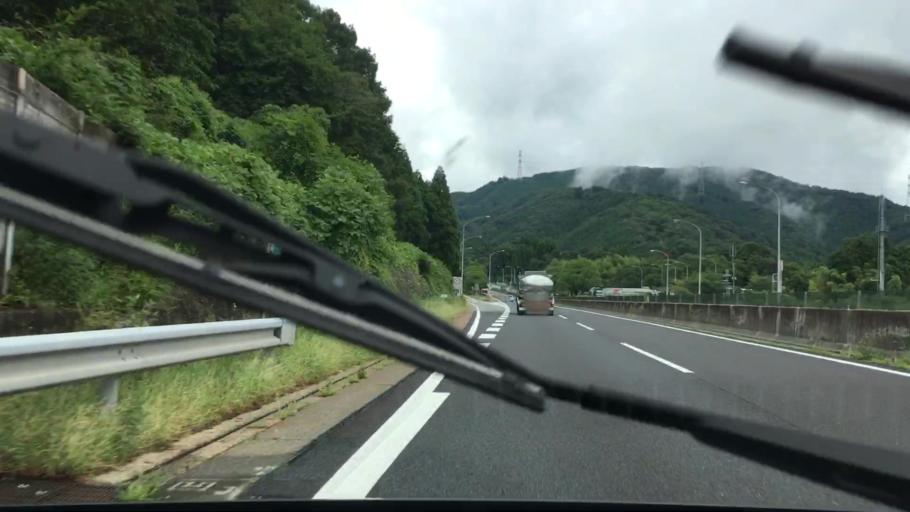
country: JP
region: Hyogo
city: Yamazakicho-nakabirose
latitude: 35.0291
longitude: 134.4884
